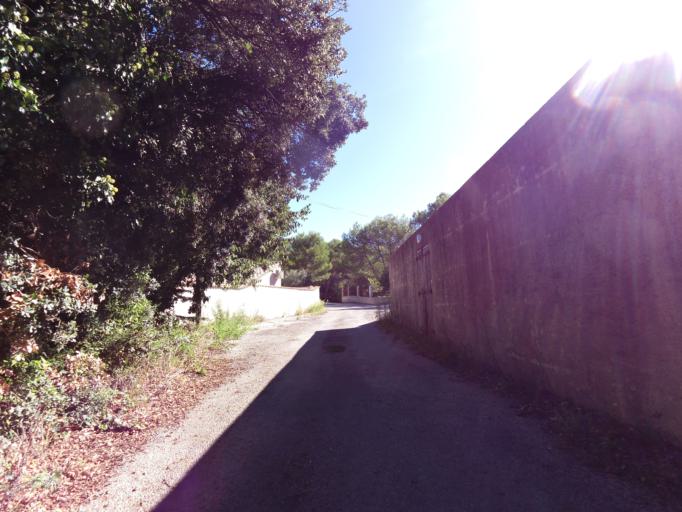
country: FR
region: Languedoc-Roussillon
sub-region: Departement du Gard
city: Aubais
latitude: 43.7475
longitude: 4.1410
